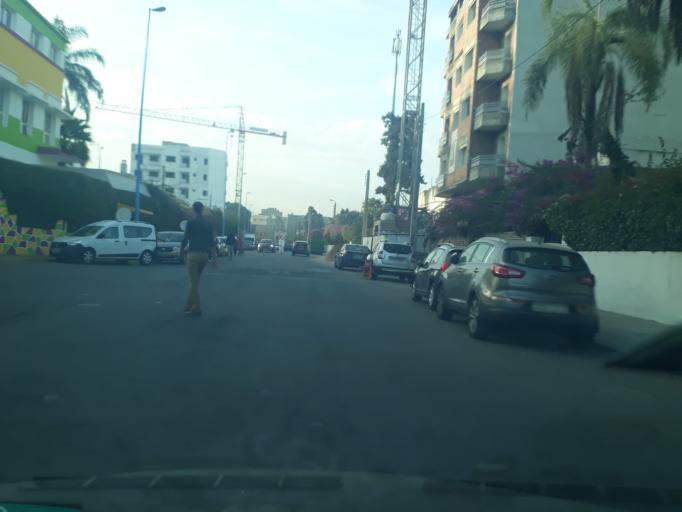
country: MA
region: Grand Casablanca
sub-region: Casablanca
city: Casablanca
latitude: 33.5800
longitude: -7.6302
